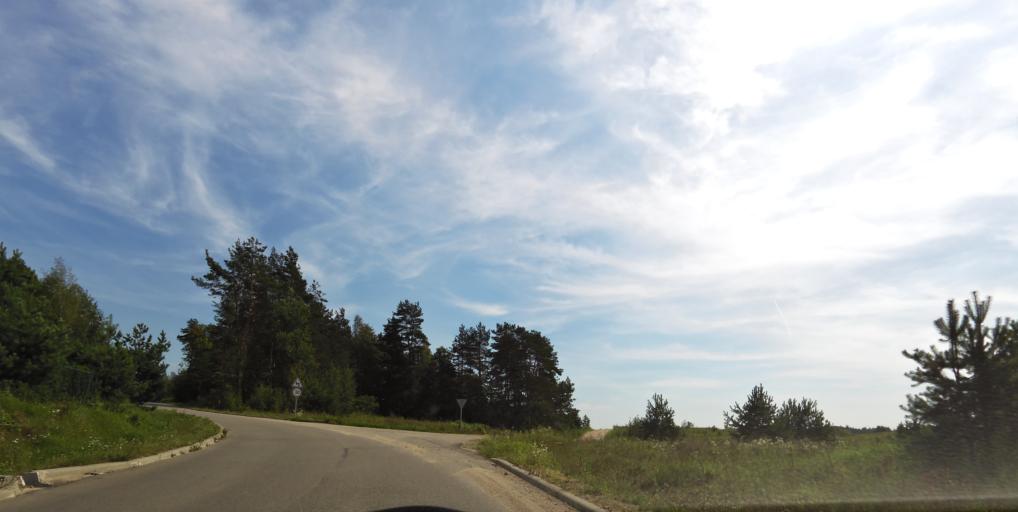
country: LT
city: Grigiskes
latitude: 54.7253
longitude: 25.0758
